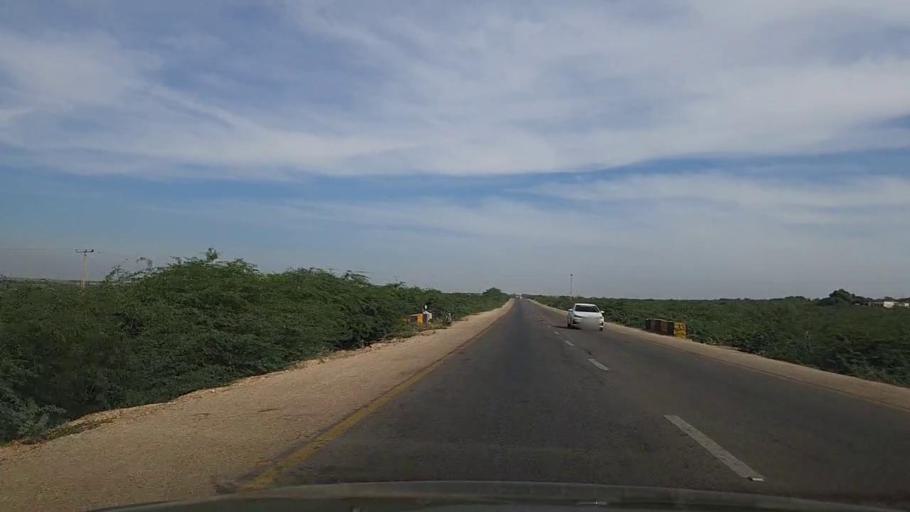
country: PK
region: Sindh
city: Thatta
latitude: 24.8395
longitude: 68.0043
